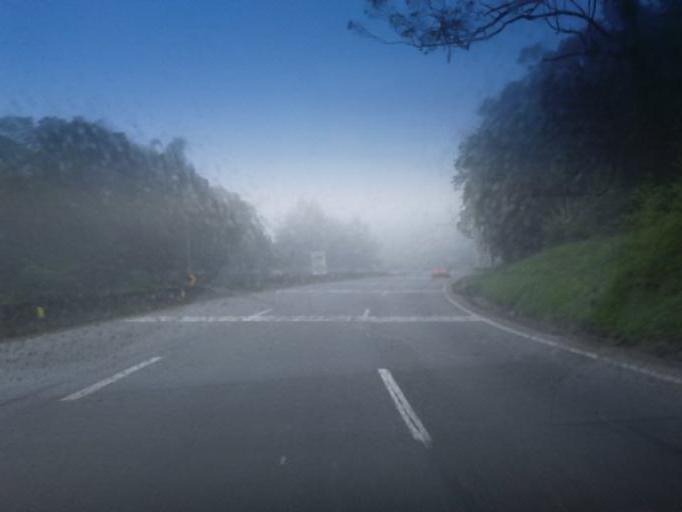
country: BR
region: Parana
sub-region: Guaratuba
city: Guaratuba
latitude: -25.8544
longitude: -48.9573
